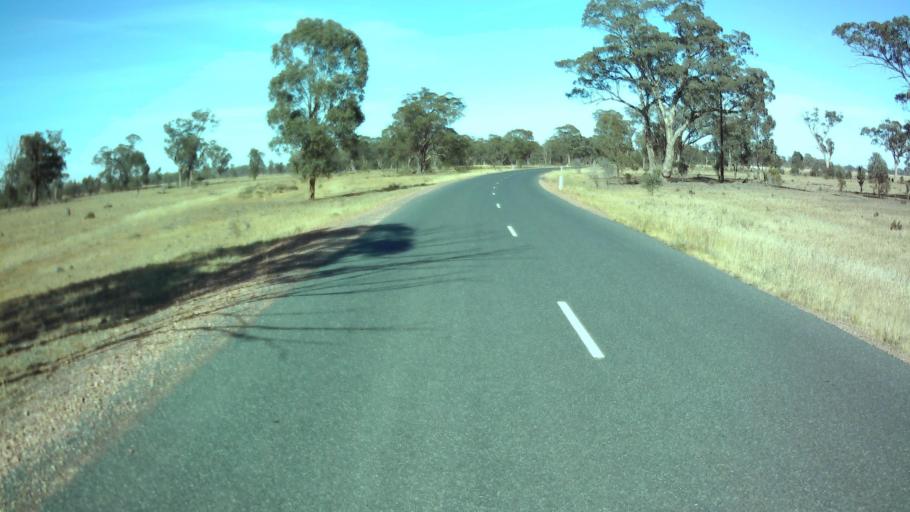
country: AU
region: New South Wales
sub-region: Weddin
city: Grenfell
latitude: -34.1124
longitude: 147.8480
